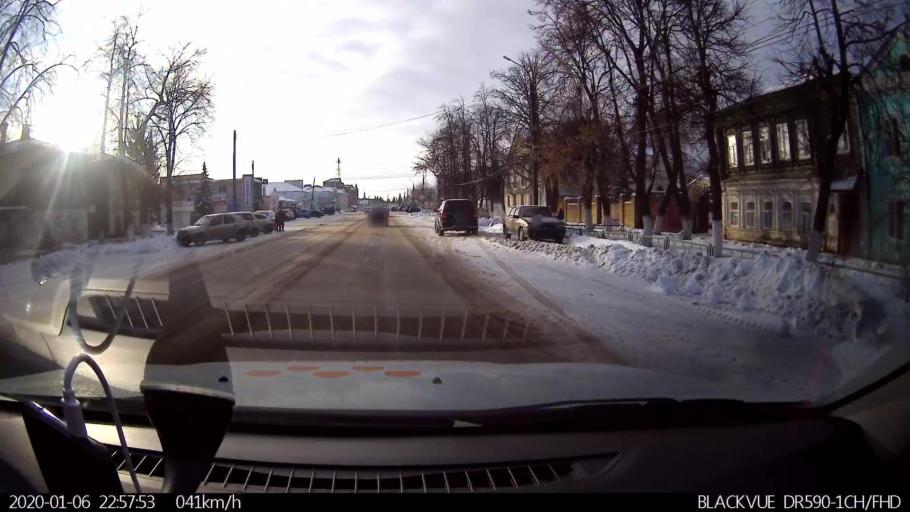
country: RU
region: Nizjnij Novgorod
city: Bogorodsk
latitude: 56.1056
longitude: 43.5203
